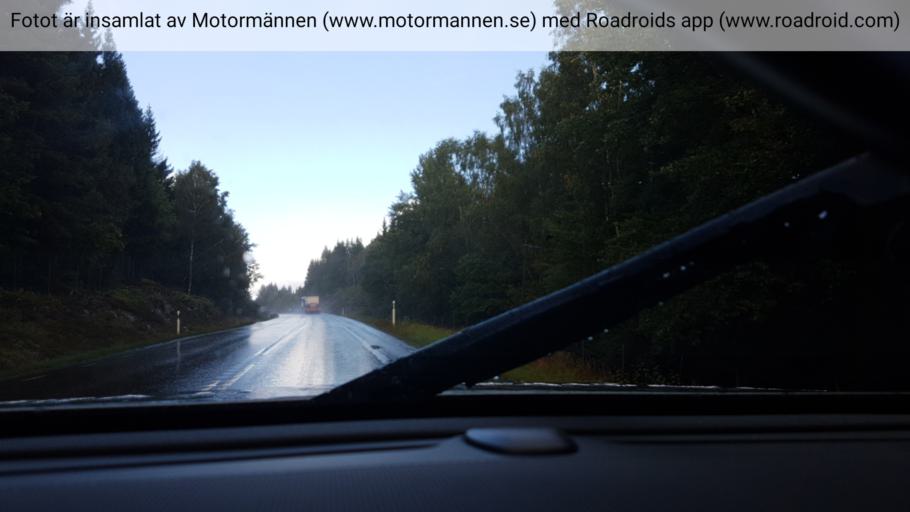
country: SE
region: Vaestra Goetaland
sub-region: Alingsas Kommun
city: Alingsas
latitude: 57.9978
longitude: 12.4435
